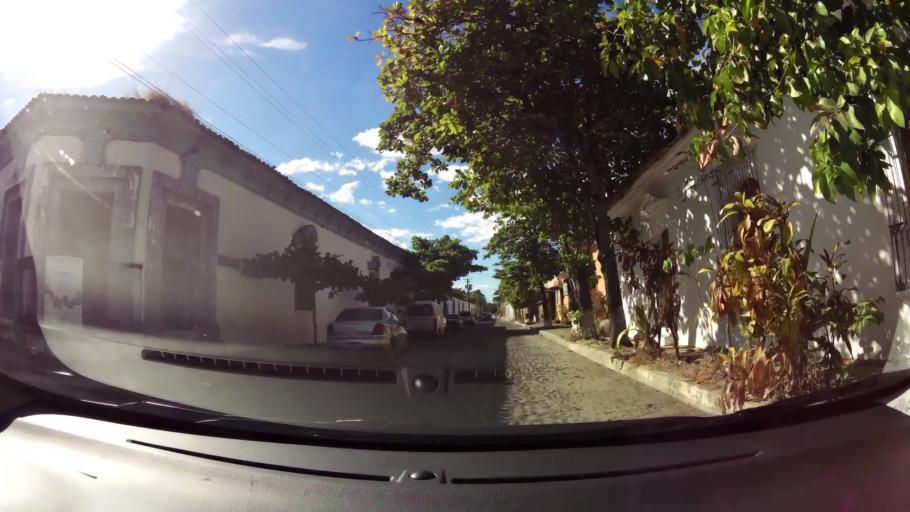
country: SV
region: Cuscatlan
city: Suchitoto
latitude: 13.9378
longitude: -89.0259
